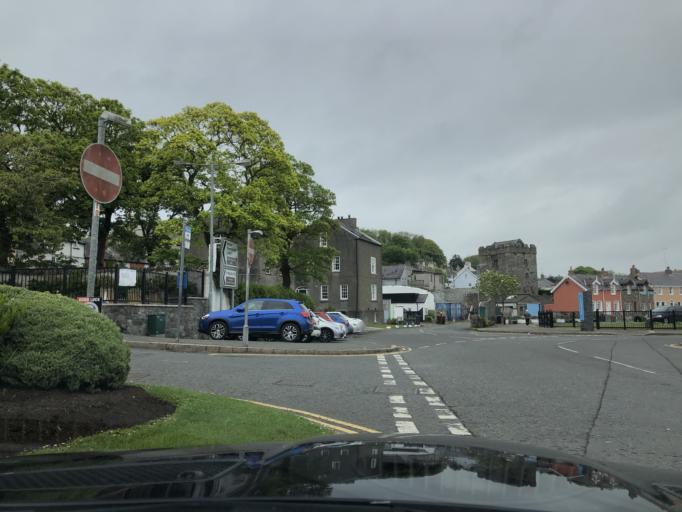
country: GB
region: Northern Ireland
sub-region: Down District
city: Portaferry
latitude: 54.3709
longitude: -5.5561
